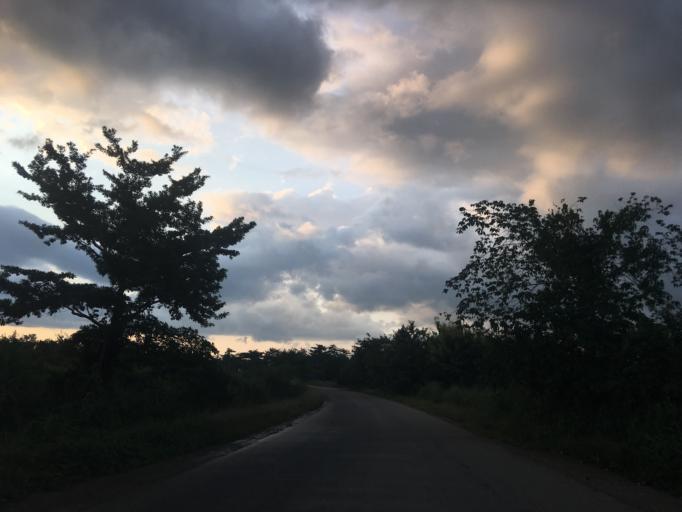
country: GH
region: Western
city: Bibiani
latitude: 6.7613
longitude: -2.5043
